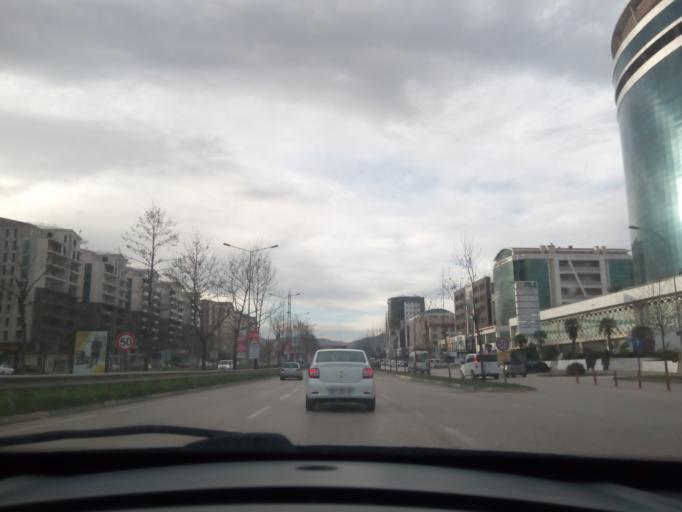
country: TR
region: Bursa
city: Cali
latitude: 40.2200
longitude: 28.9523
